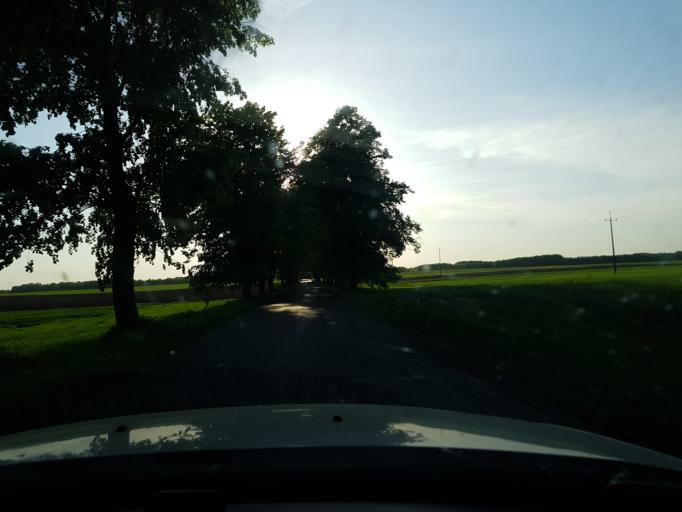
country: PL
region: West Pomeranian Voivodeship
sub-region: Powiat goleniowski
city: Maszewo
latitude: 53.4790
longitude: 15.0109
